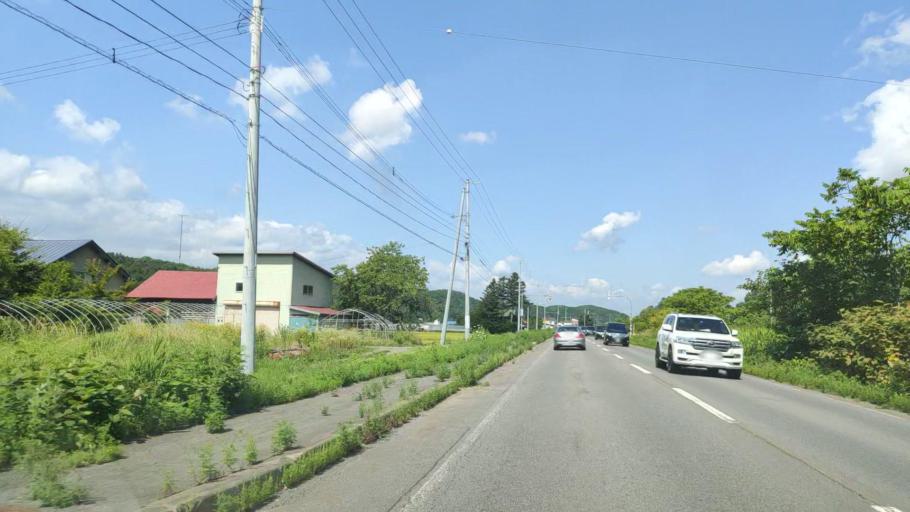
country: JP
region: Hokkaido
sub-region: Asahikawa-shi
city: Asahikawa
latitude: 43.6302
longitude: 142.4616
